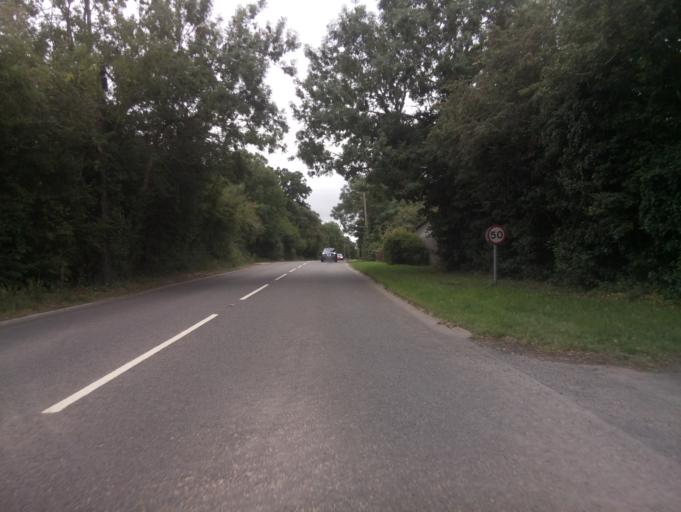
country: GB
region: England
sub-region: Gloucestershire
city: Tewkesbury
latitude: 52.0104
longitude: -2.1617
